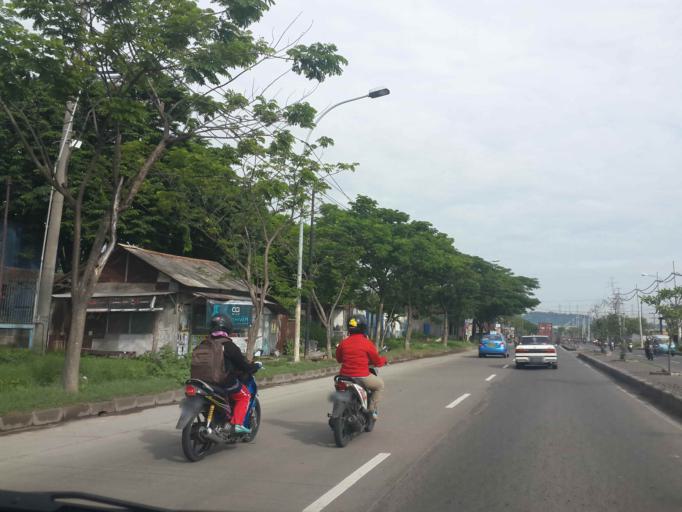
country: ID
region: East Java
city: Kebomas
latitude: -7.2047
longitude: 112.6502
